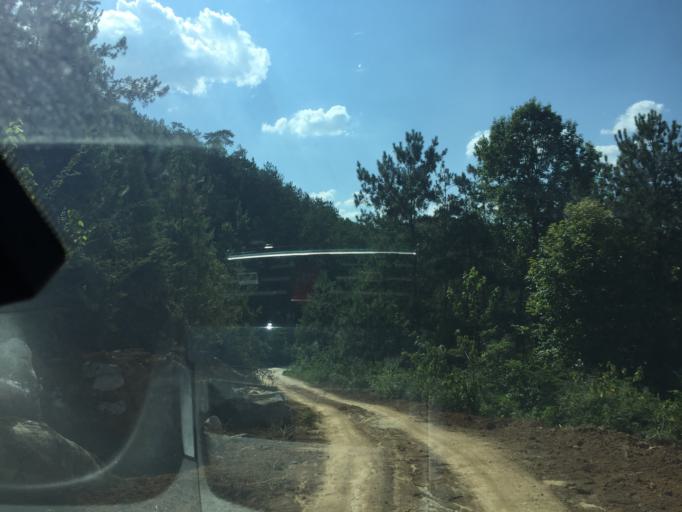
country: CN
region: Guizhou Sheng
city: Jiashi
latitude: 28.3363
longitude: 108.3095
